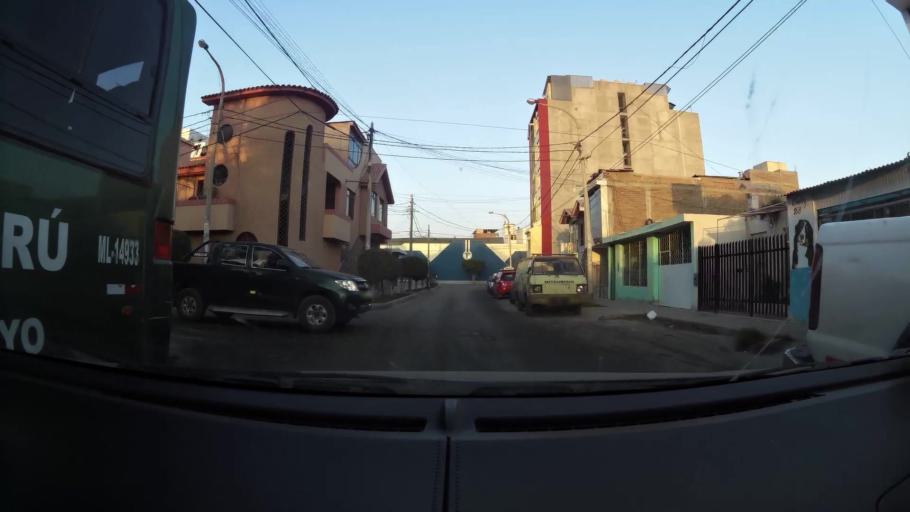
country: PE
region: Lambayeque
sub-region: Provincia de Chiclayo
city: Santa Rosa
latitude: -6.7677
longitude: -79.8333
